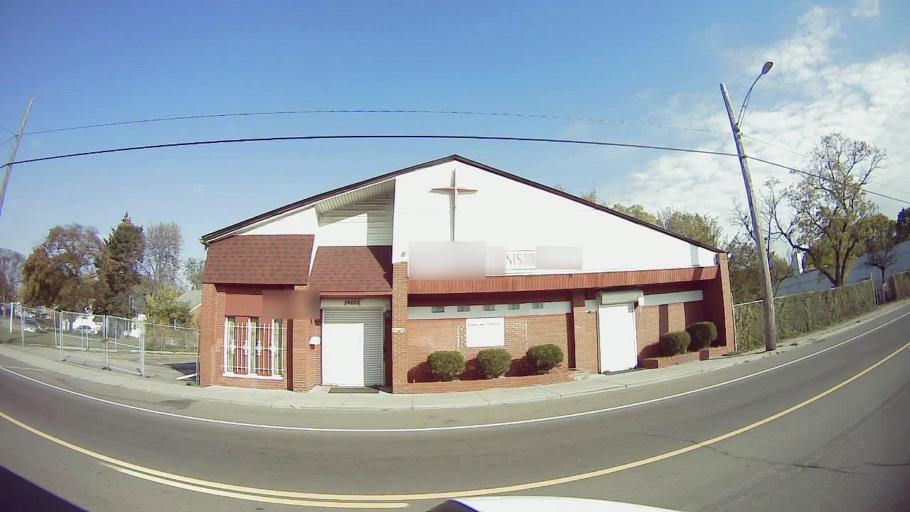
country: US
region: Michigan
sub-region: Wayne County
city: Highland Park
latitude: 42.4345
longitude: -83.0749
